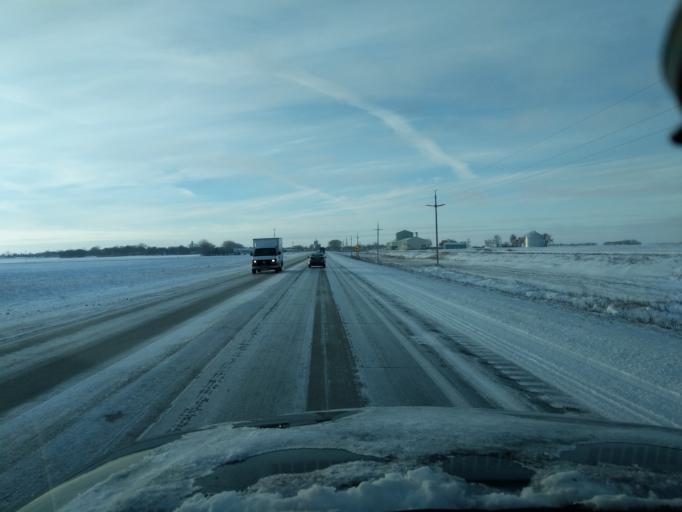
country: US
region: Minnesota
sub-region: Renville County
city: Bird Island
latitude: 44.7651
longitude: -94.8697
